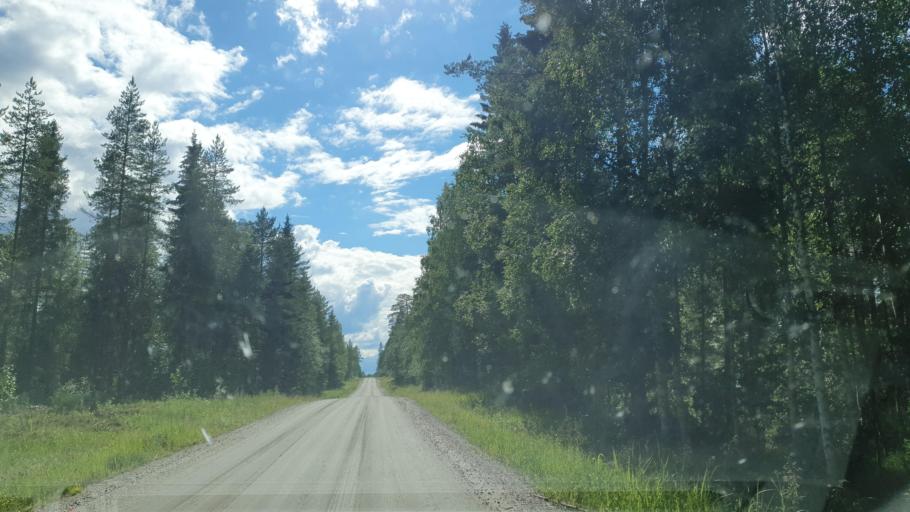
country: FI
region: Kainuu
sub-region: Kehys-Kainuu
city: Kuhmo
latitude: 64.1500
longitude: 29.7268
